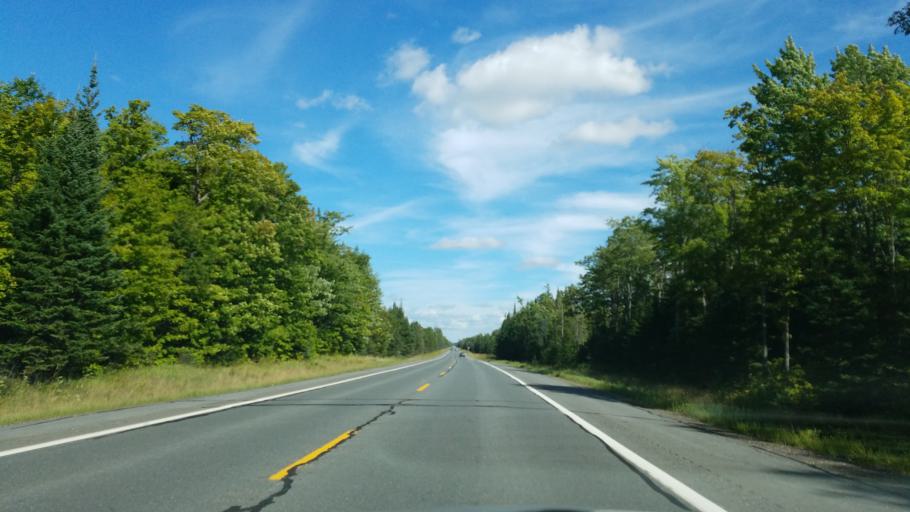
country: US
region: Michigan
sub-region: Baraga County
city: L'Anse
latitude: 46.5788
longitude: -88.4475
